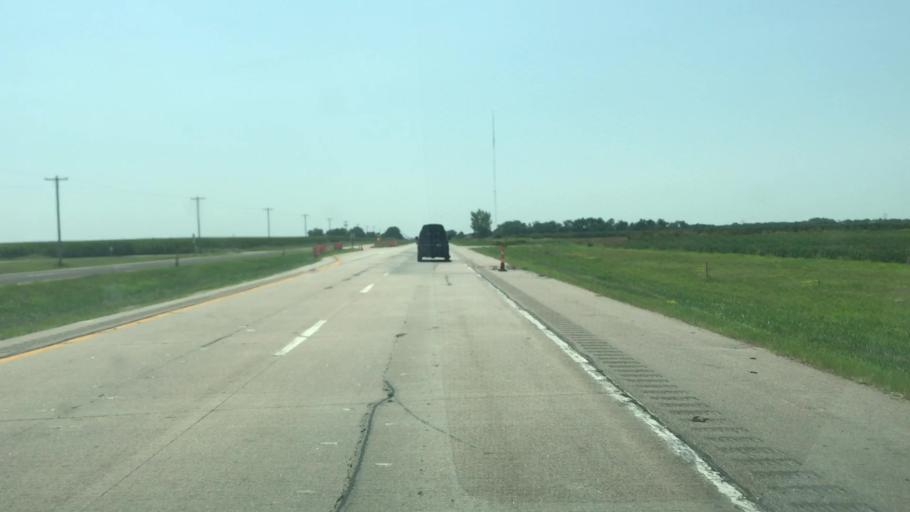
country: US
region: Nebraska
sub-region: Adams County
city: Hastings
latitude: 40.6637
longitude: -98.3824
